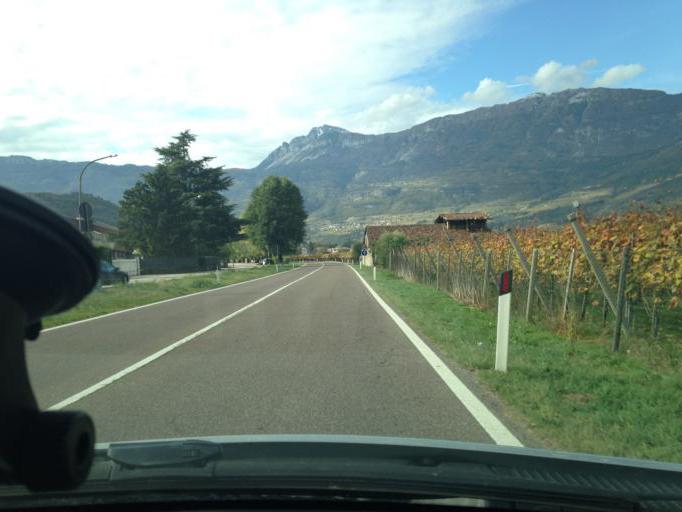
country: IT
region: Trentino-Alto Adige
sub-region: Provincia di Trento
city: Nomi
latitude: 45.9181
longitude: 11.0784
